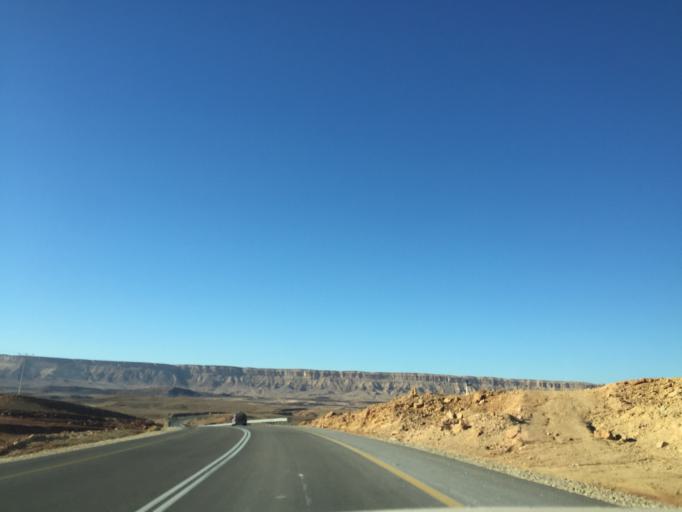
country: IL
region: Southern District
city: Mitzpe Ramon
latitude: 30.6032
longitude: 34.8701
